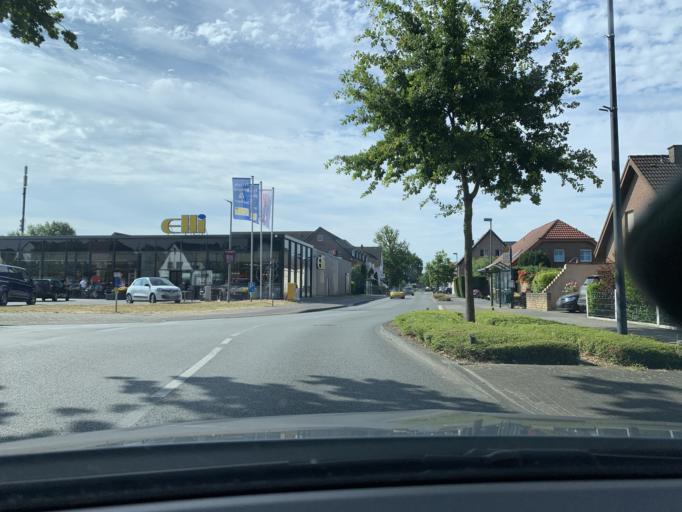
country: DE
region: North Rhine-Westphalia
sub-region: Regierungsbezirk Arnsberg
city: Lippstadt
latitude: 51.6961
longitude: 8.3757
